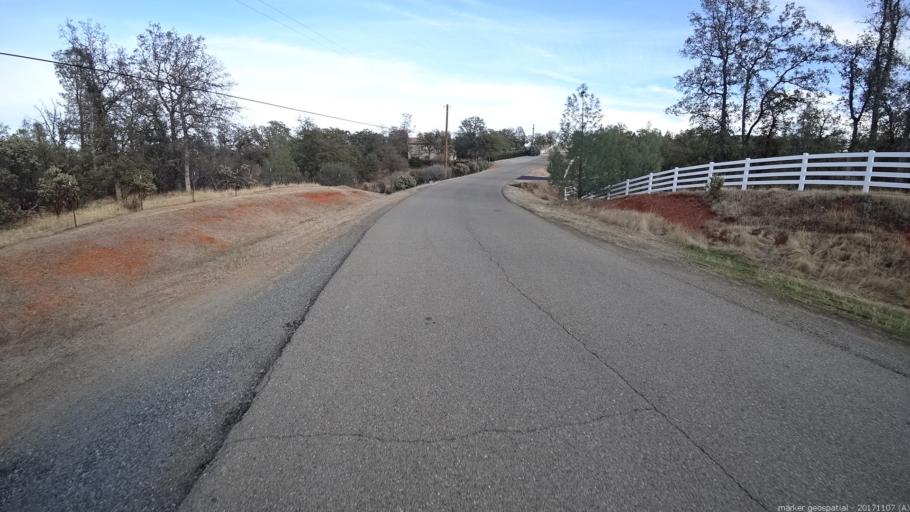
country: US
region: California
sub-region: Shasta County
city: Shasta
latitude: 40.5157
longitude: -122.4811
